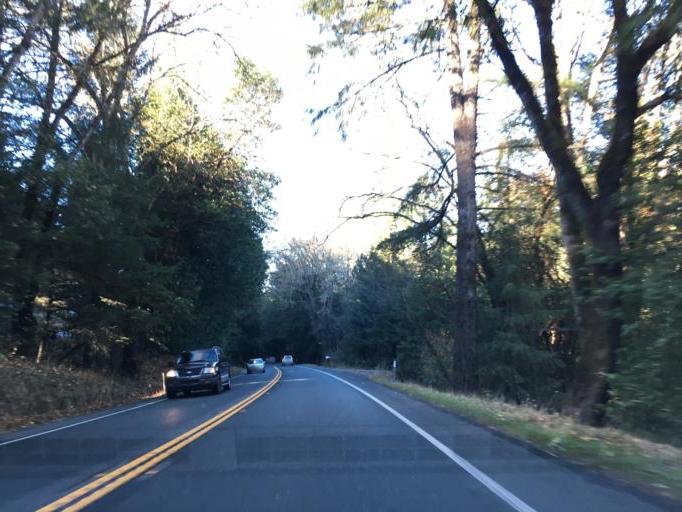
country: US
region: California
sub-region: Mendocino County
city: Brooktrails
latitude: 39.4927
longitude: -123.3638
